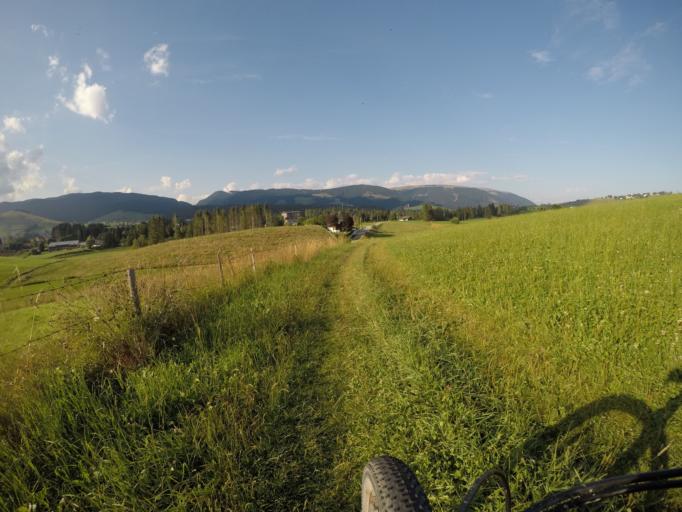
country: IT
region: Veneto
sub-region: Provincia di Vicenza
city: Asiago
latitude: 45.8757
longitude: 11.5244
